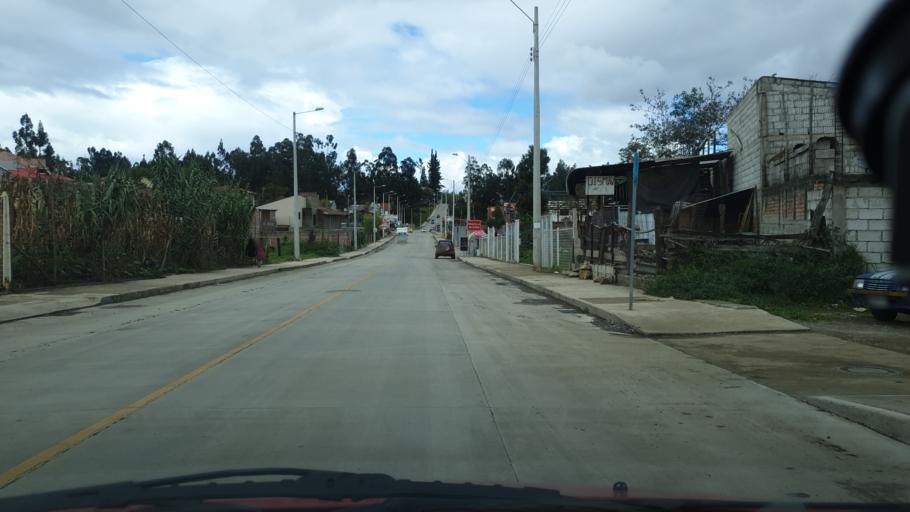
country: EC
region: Azuay
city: Cuenca
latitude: -2.8816
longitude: -79.0574
